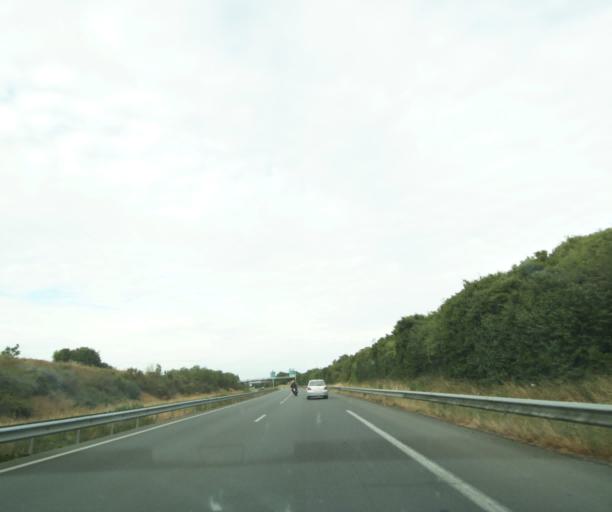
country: FR
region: Poitou-Charentes
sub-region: Departement de la Charente-Maritime
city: Sainte-Soulle
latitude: 46.1997
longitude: -1.0334
